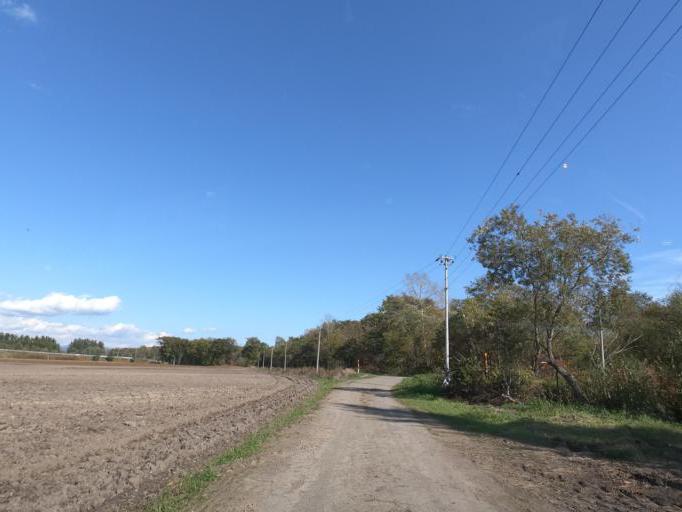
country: JP
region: Hokkaido
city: Otofuke
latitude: 43.2348
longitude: 143.2652
